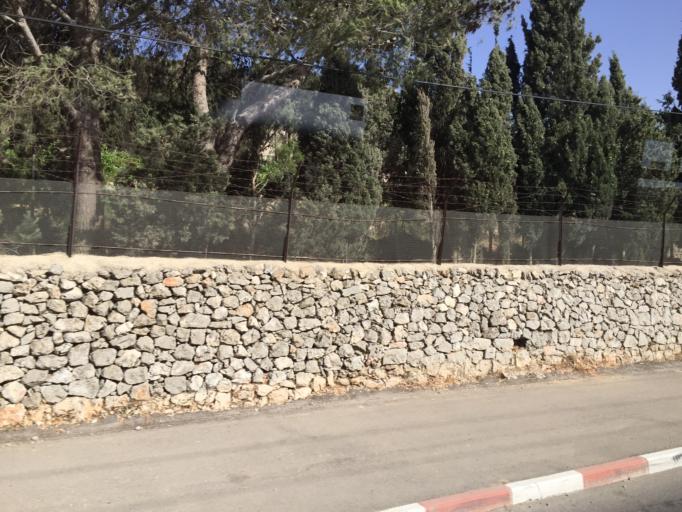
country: PS
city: Ad Dawhah
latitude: 31.7092
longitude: 35.1729
